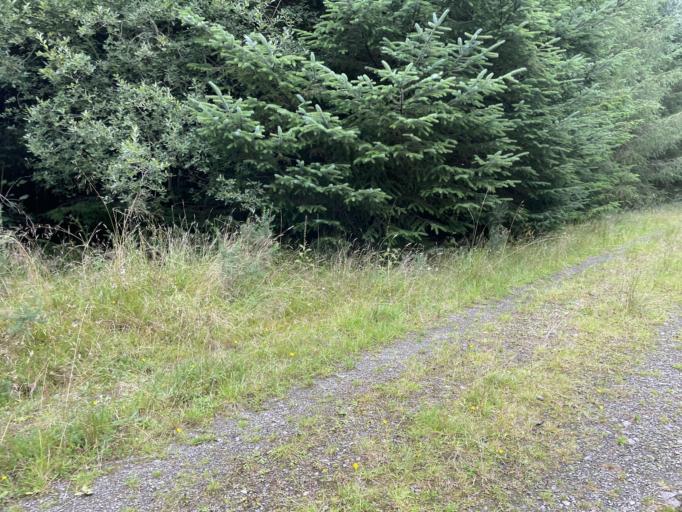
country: GB
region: Scotland
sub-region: South Ayrshire
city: Maybole
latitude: 55.2006
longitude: -4.6720
